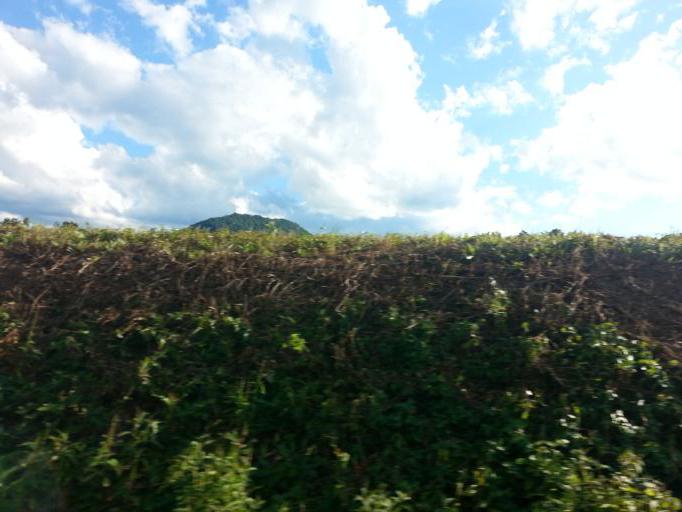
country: US
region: Tennessee
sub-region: Union County
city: Condon
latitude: 36.1421
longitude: -83.7574
